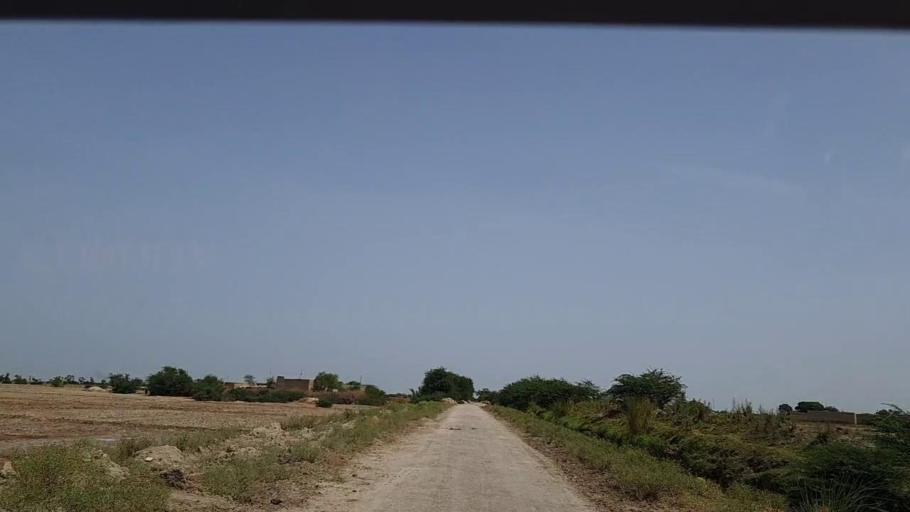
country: PK
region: Sindh
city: Johi
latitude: 26.7774
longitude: 67.6232
